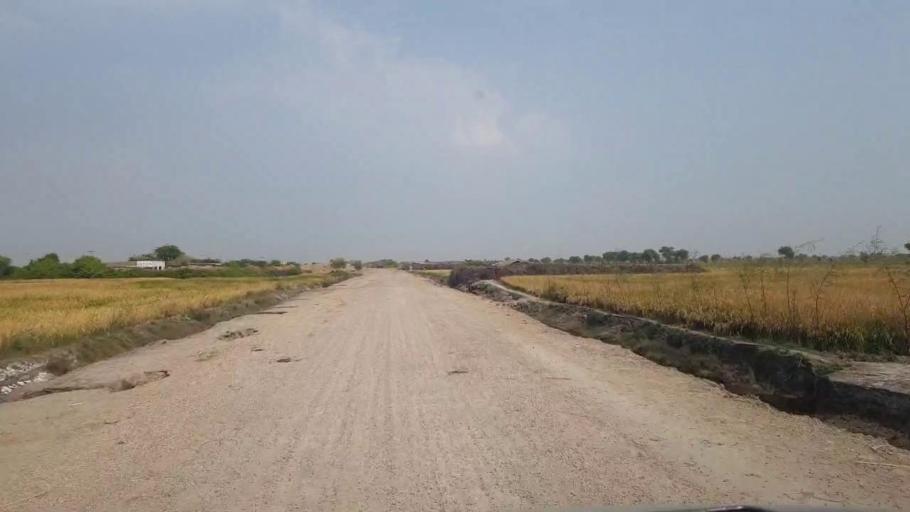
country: PK
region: Sindh
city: Matli
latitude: 24.9613
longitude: 68.6870
